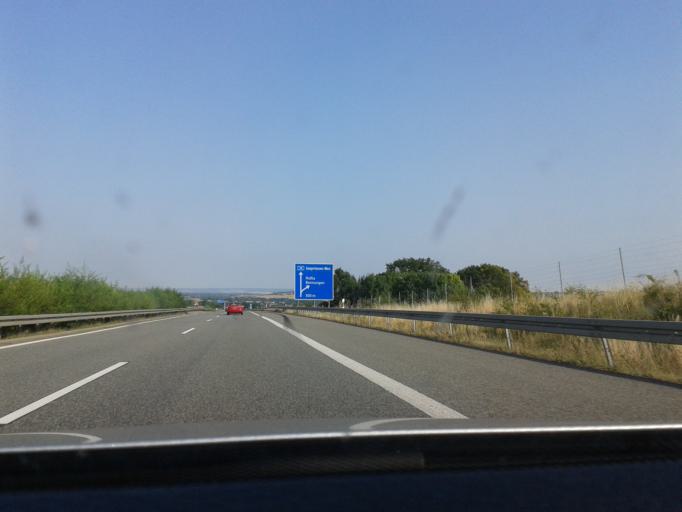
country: DE
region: Saxony-Anhalt
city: Rossla
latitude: 51.4721
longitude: 11.0868
